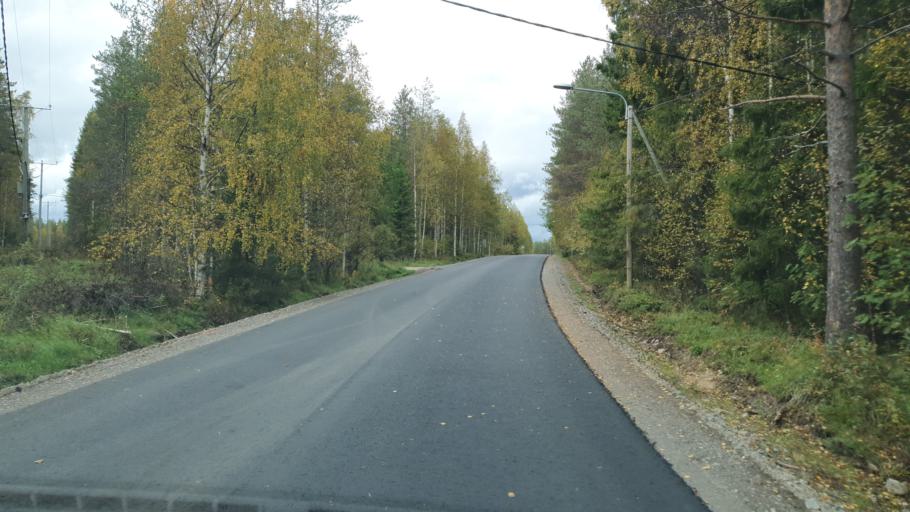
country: FI
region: Lapland
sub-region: Rovaniemi
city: Rovaniemi
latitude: 66.4211
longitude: 25.4061
